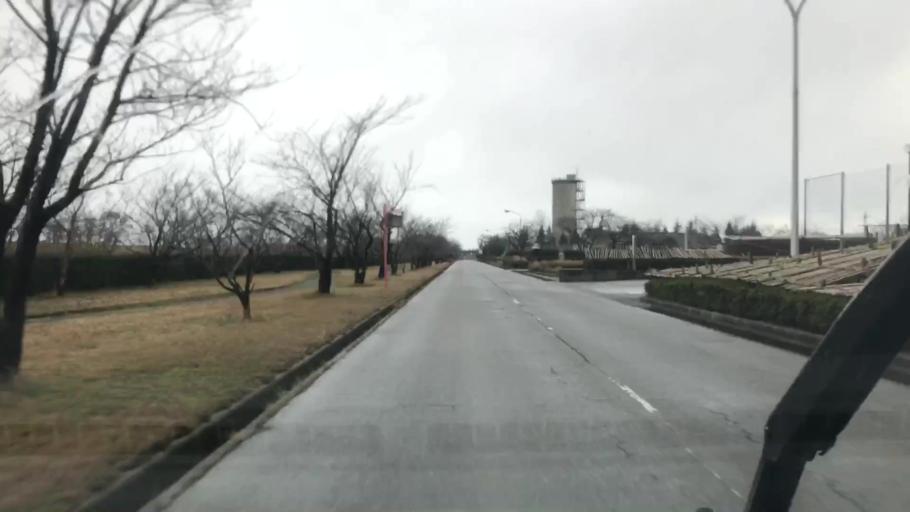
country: JP
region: Toyama
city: Kamiichi
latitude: 36.6215
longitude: 137.3040
